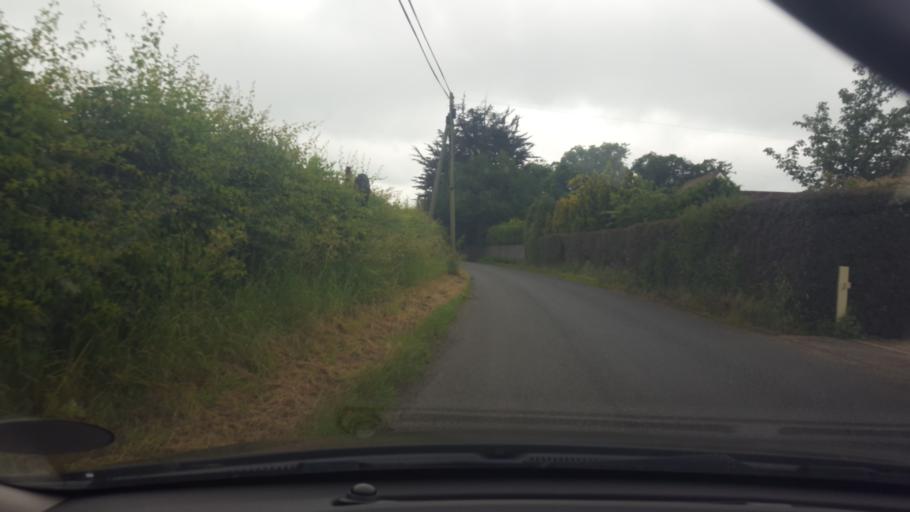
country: GB
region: England
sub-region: Essex
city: Great Bentley
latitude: 51.8757
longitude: 1.0813
